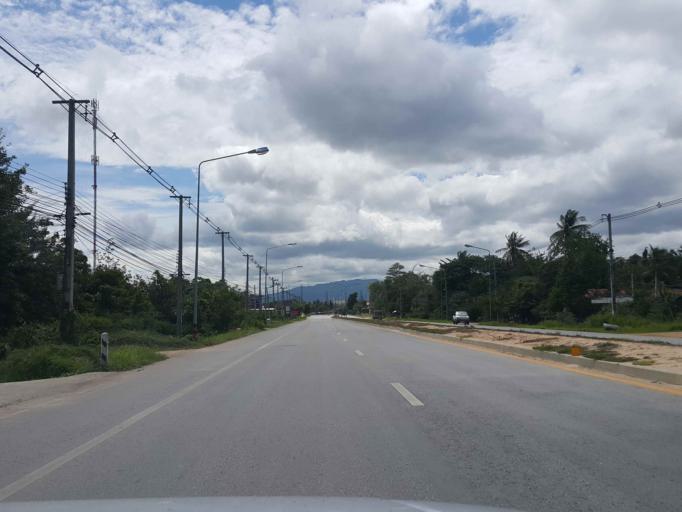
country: TH
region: Tak
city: Tak
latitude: 16.8874
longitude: 99.1721
